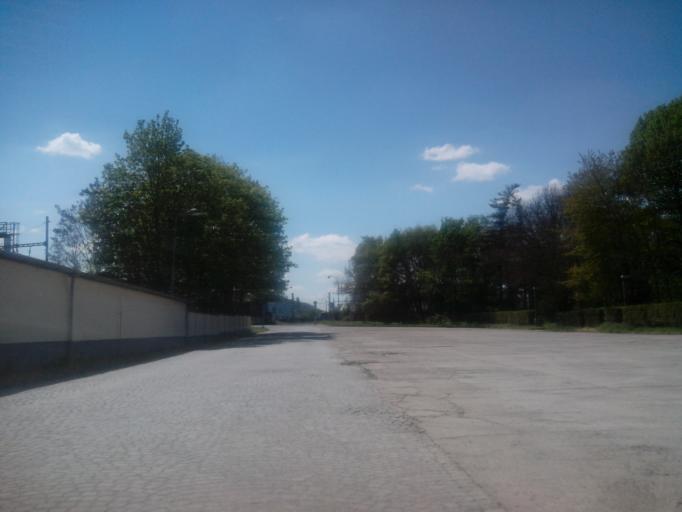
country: CZ
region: Central Bohemia
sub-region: Okres Beroun
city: Kraluv Dvur
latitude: 49.9464
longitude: 14.0474
